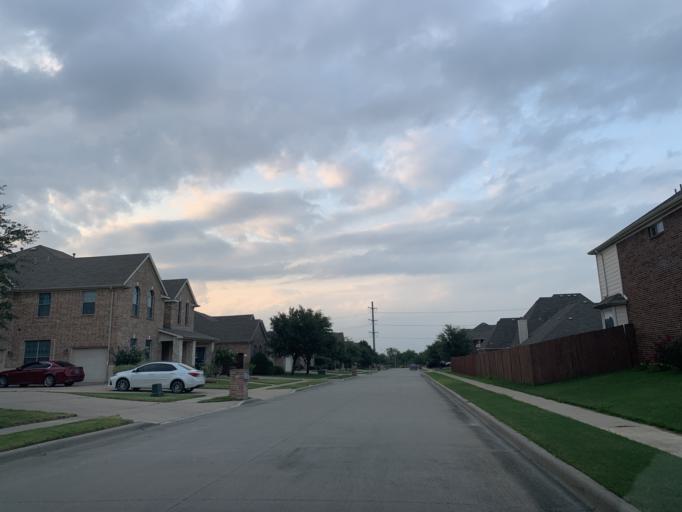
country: US
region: Texas
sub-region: Tarrant County
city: Keller
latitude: 32.9251
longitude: -97.2718
